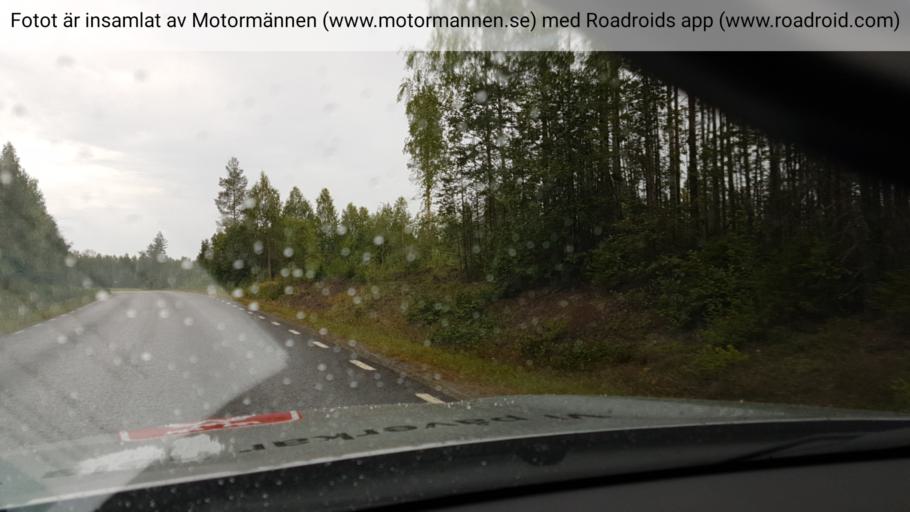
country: SE
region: Norrbotten
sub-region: Bodens Kommun
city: Boden
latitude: 65.8813
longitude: 21.3747
